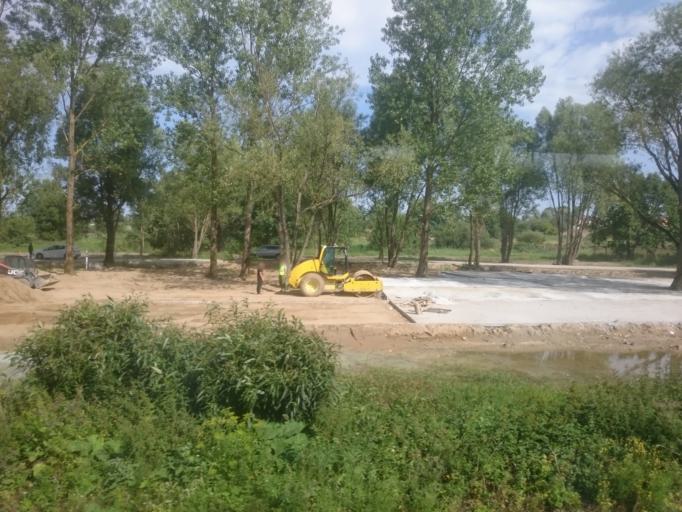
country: RU
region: Kaliningrad
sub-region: Zelenogradskiy Rayon
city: Zelenogradsk
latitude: 54.9507
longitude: 20.4501
